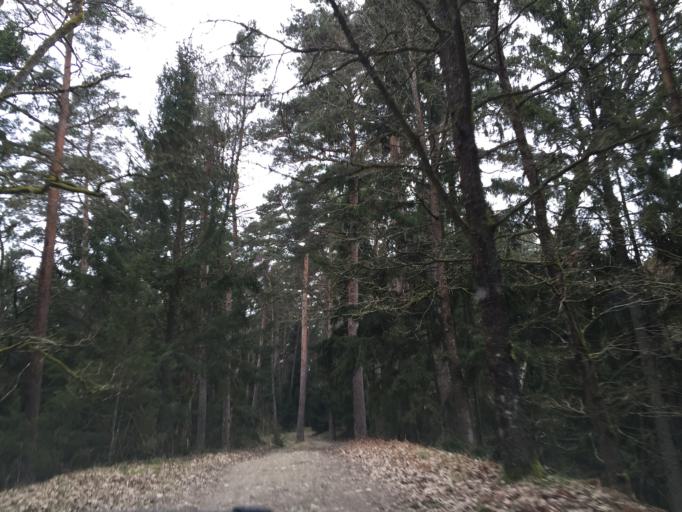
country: LT
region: Klaipedos apskritis
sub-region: Klaipeda
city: Klaipeda
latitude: 55.5552
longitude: 21.1200
